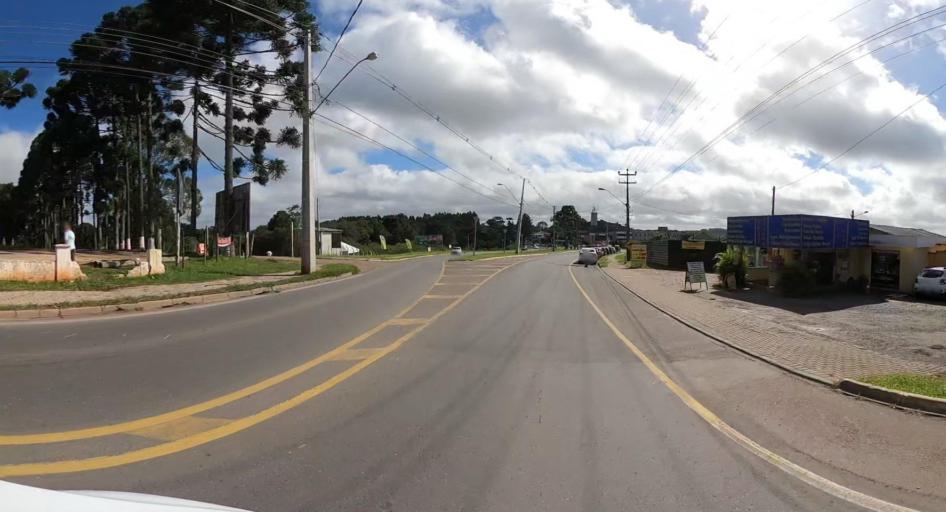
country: BR
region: Parana
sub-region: Quatro Barras
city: Quatro Barras
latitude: -25.3536
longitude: -49.0830
